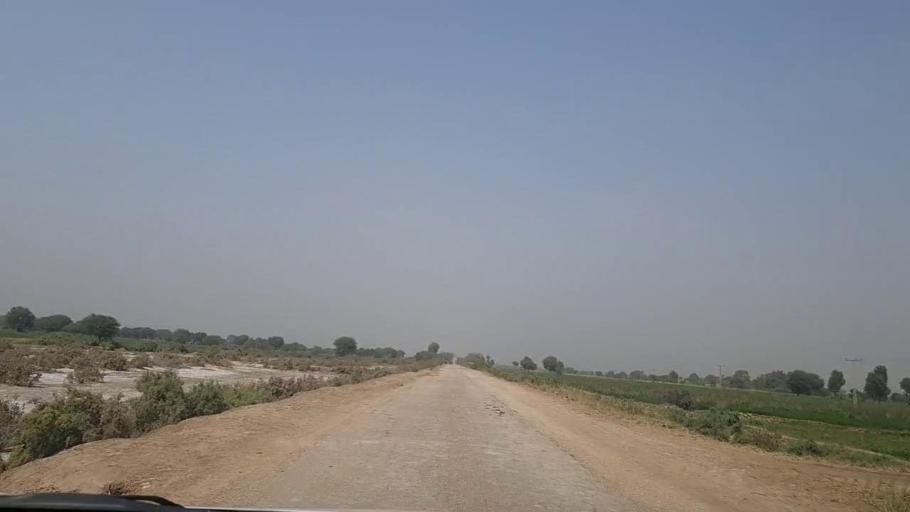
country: PK
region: Sindh
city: Pithoro
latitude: 25.5808
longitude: 69.2011
